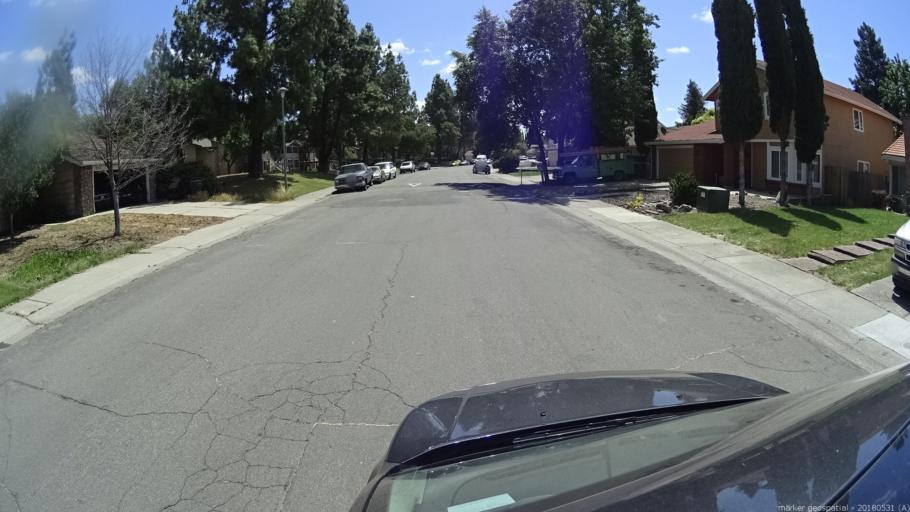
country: US
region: California
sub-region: Sacramento County
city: Sacramento
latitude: 38.6260
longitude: -121.5117
